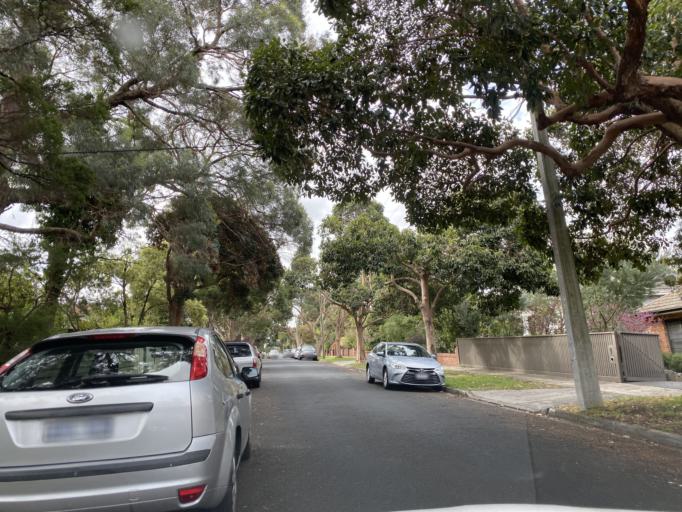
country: AU
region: Victoria
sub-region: Whitehorse
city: Burwood
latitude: -37.8492
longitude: 145.1024
